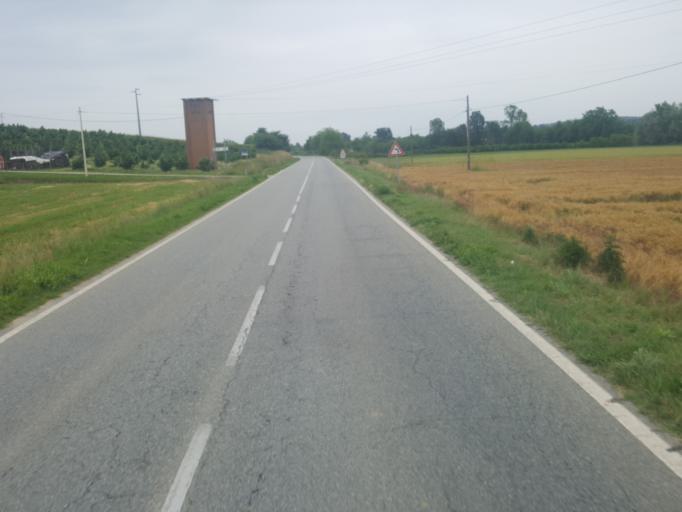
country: IT
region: Piedmont
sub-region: Provincia di Torino
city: Pralormo
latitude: 44.8390
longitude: 7.9143
